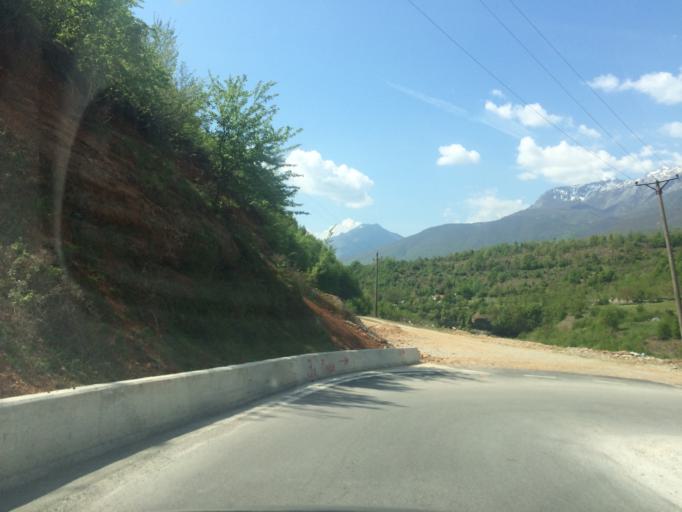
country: AL
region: Kukes
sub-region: Rrethi i Tropojes
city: Llugaj
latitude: 42.3527
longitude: 20.0946
